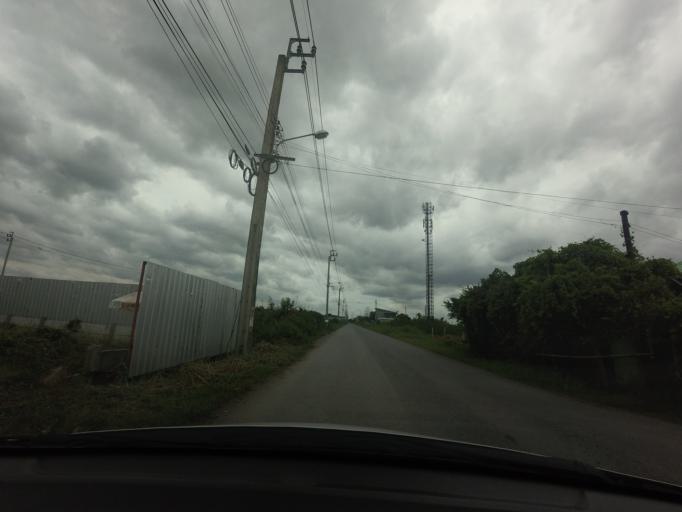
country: TH
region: Bangkok
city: Min Buri
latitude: 13.7754
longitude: 100.7671
